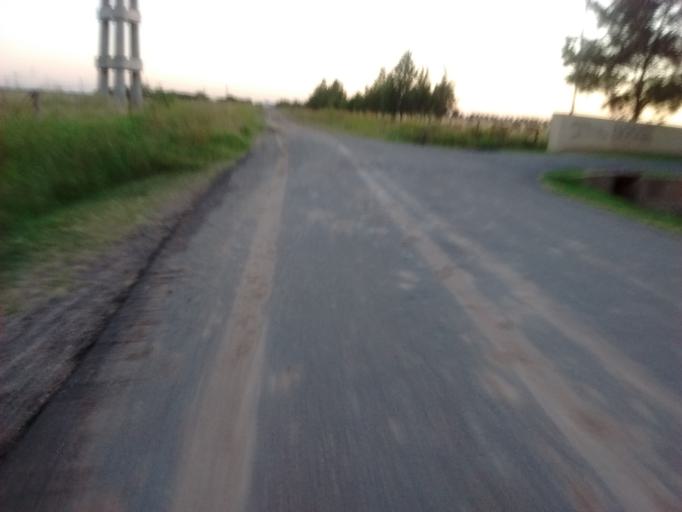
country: AR
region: Santa Fe
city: Funes
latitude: -32.9527
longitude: -60.8194
